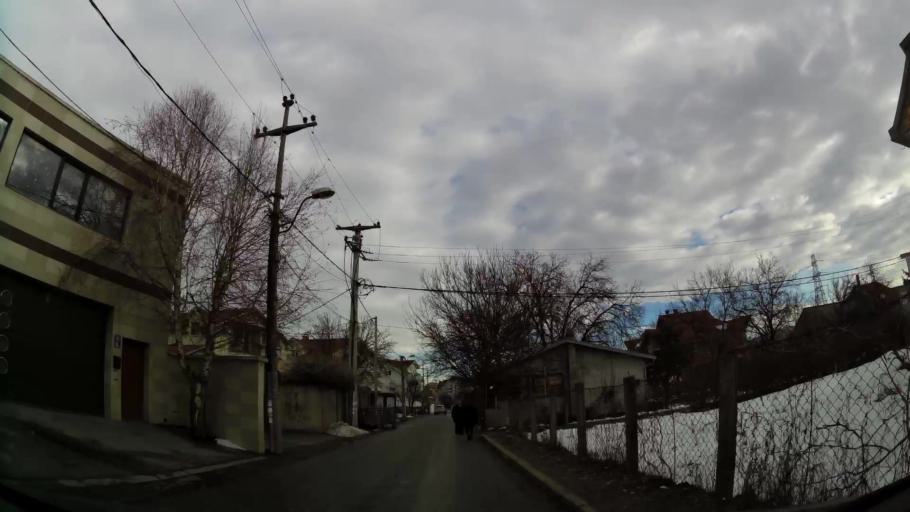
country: RS
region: Central Serbia
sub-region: Belgrade
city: Zemun
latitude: 44.8065
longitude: 20.3589
